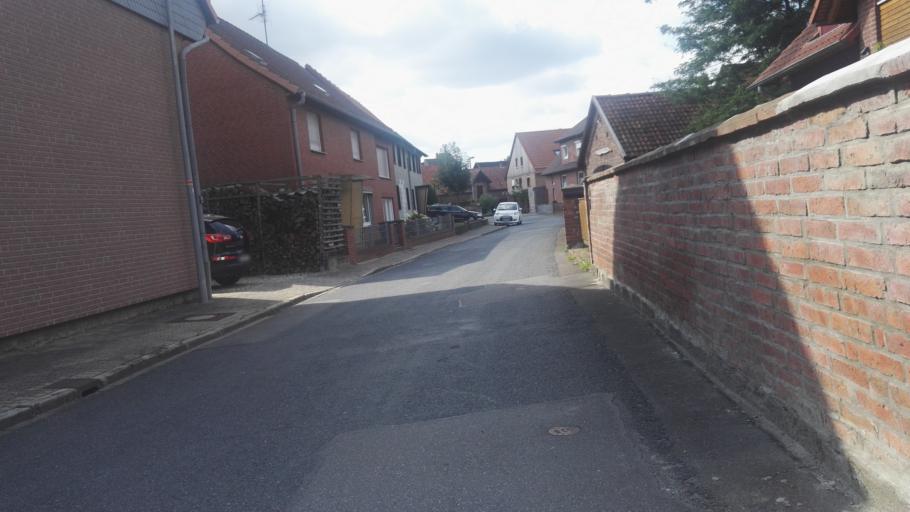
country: DE
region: Lower Saxony
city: Schellerten
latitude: 52.1676
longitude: 10.0621
